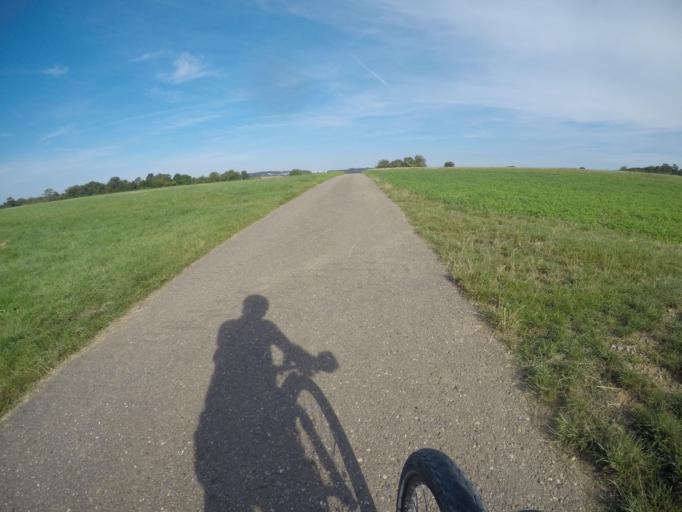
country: DE
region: Baden-Wuerttemberg
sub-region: Regierungsbezirk Stuttgart
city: Weissach
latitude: 48.8387
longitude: 8.9387
